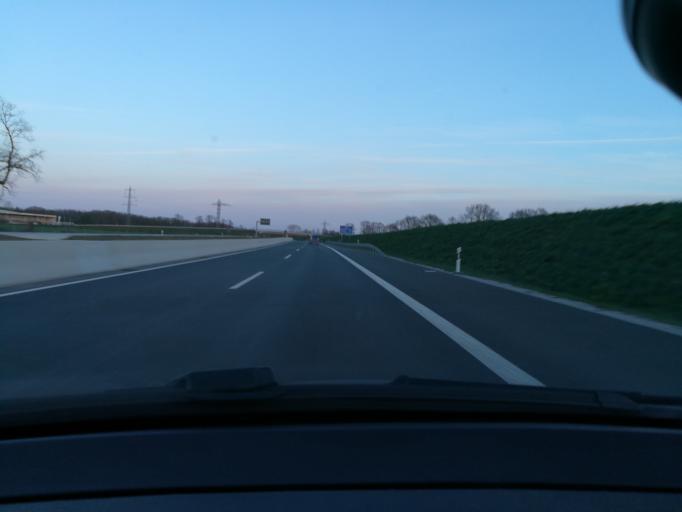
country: DE
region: North Rhine-Westphalia
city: Halle
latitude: 52.0365
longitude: 8.3452
